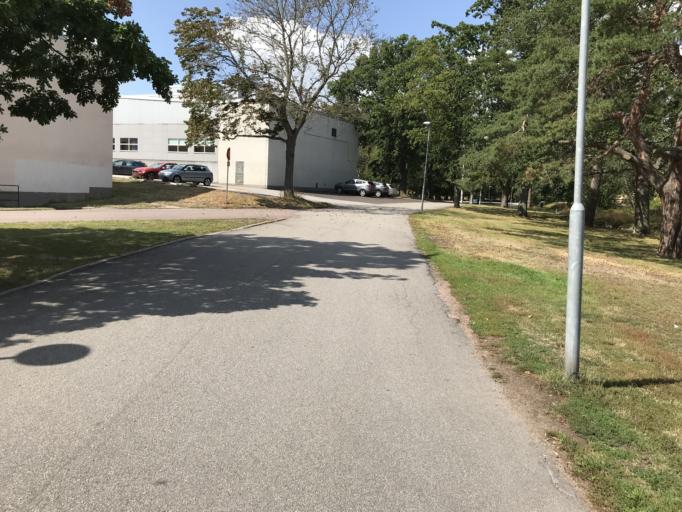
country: SE
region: Kalmar
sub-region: Oskarshamns Kommun
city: Oskarshamn
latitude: 57.2624
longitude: 16.4525
